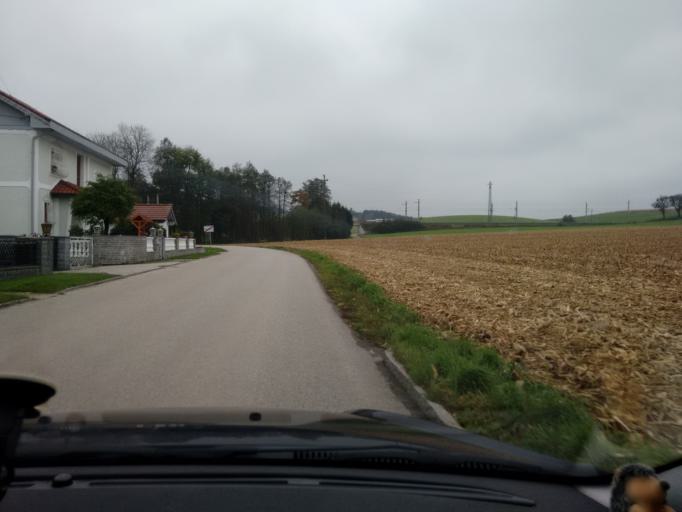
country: AT
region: Upper Austria
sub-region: Wels-Land
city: Buchkirchen
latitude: 48.1997
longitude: 13.9781
